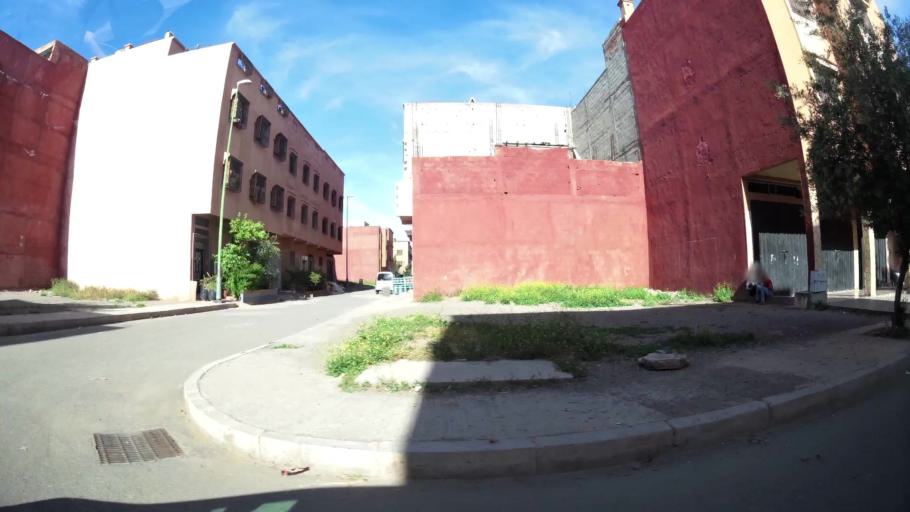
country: MA
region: Marrakech-Tensift-Al Haouz
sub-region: Marrakech
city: Marrakesh
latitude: 31.6847
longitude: -8.0741
